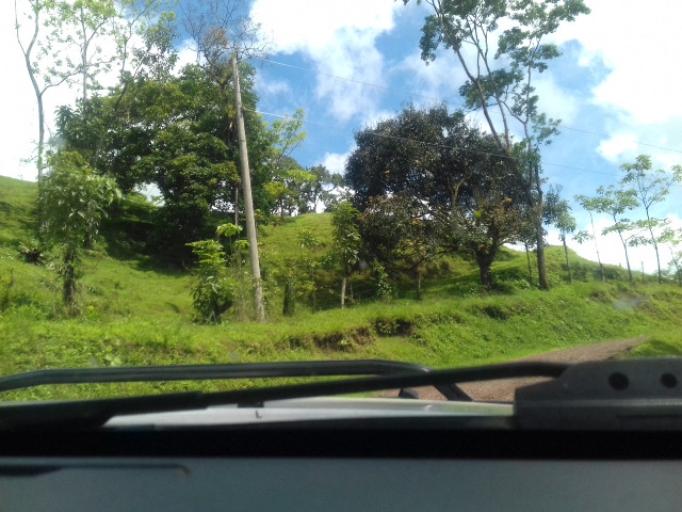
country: NI
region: Matagalpa
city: Rio Blanco
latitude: 12.9884
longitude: -85.1895
